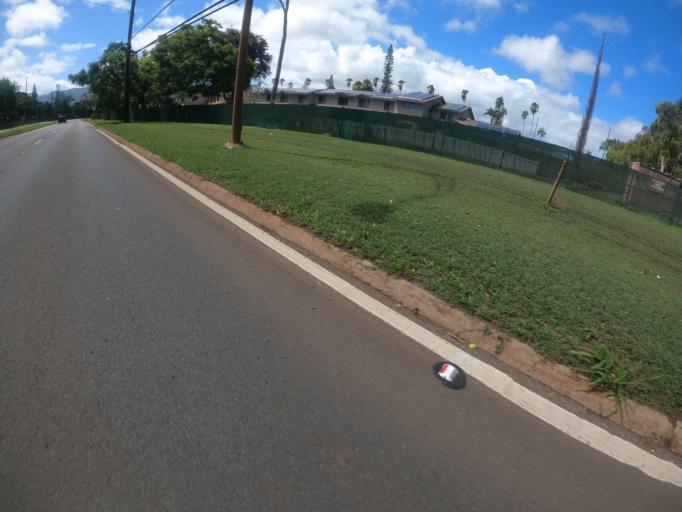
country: US
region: Hawaii
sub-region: Honolulu County
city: Wahiawa
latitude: 21.4870
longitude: -158.0412
